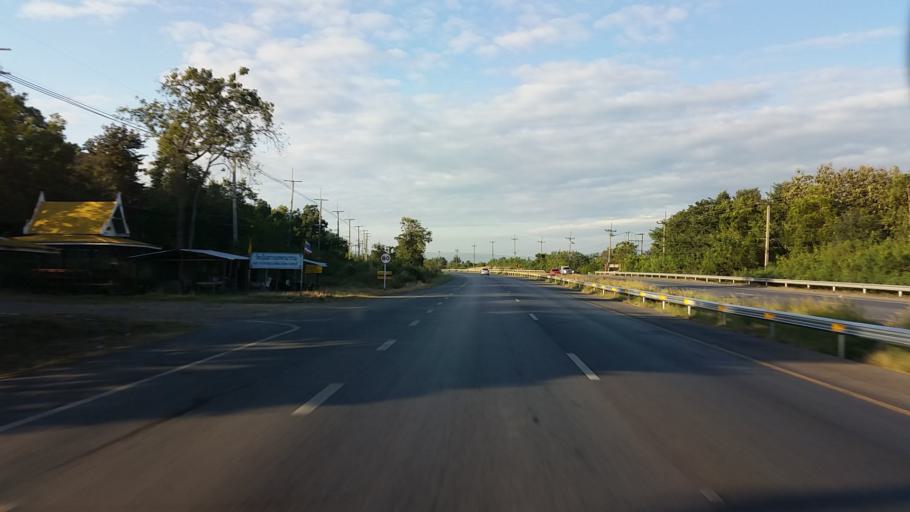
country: TH
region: Lop Buri
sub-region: Amphoe Tha Luang
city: Tha Luang
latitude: 15.0504
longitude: 100.9623
